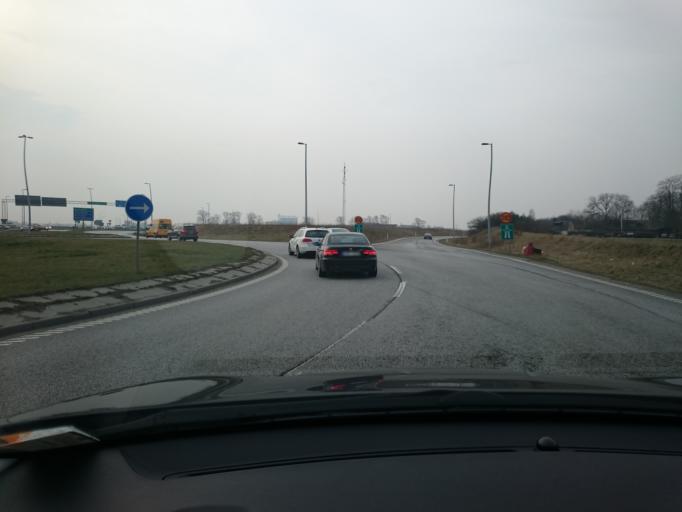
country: SE
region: Skane
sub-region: Lunds Kommun
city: Lund
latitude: 55.6794
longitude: 13.1795
